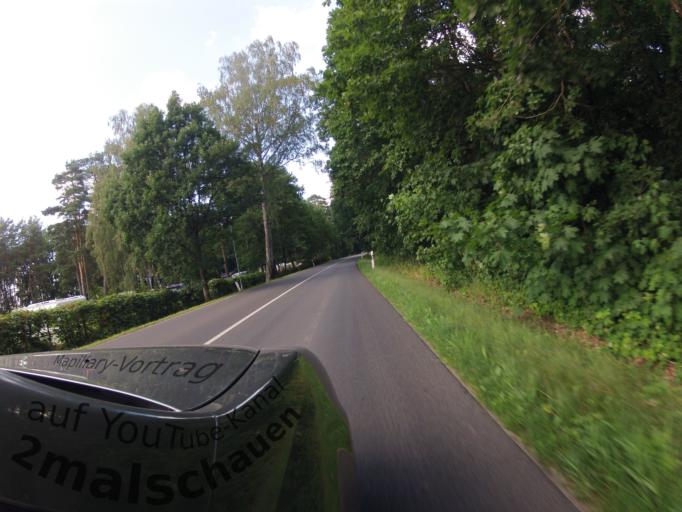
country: DE
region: Mecklenburg-Vorpommern
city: Seebad Heringsdorf
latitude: 53.9141
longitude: 14.1507
